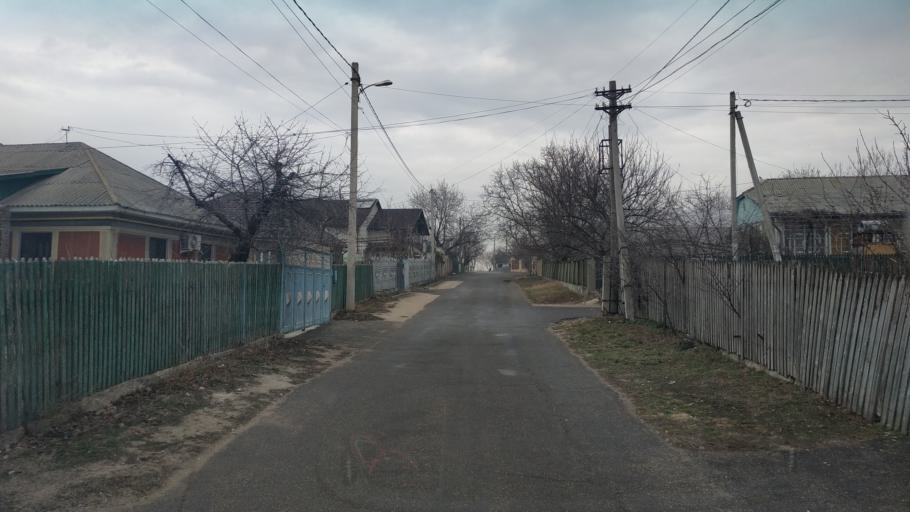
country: MD
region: Chisinau
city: Singera
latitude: 46.9192
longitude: 28.9619
